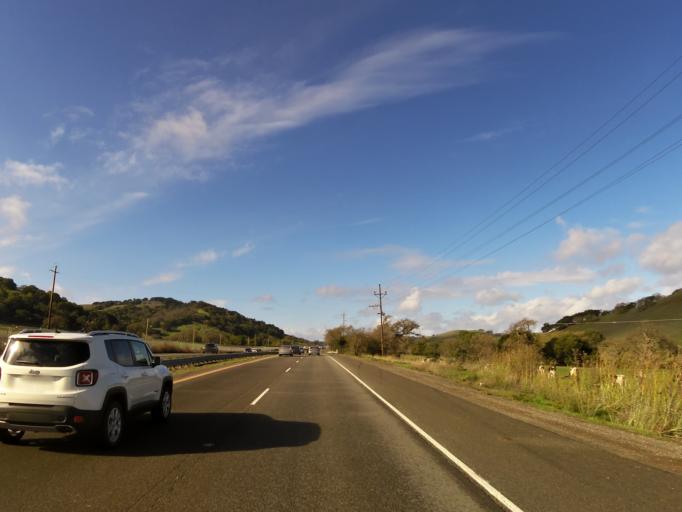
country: US
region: California
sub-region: Marin County
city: Novato
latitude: 38.1685
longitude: -122.5825
